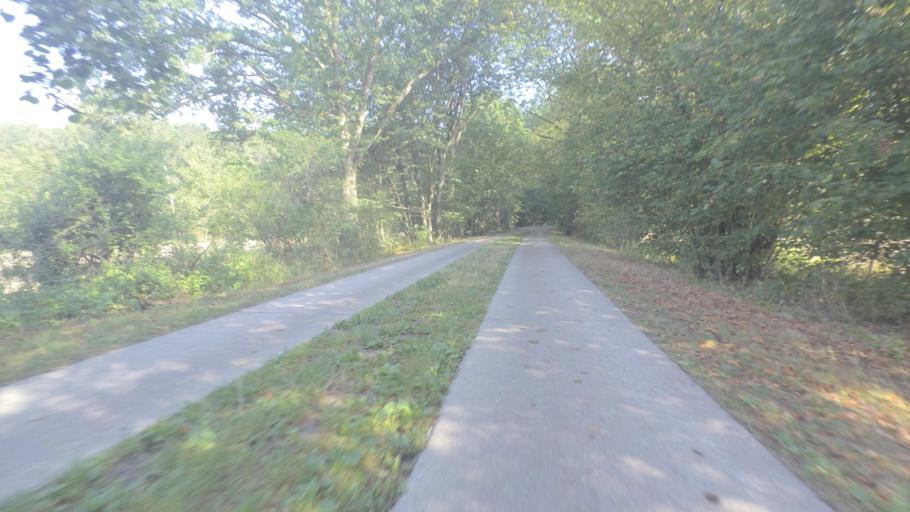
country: DE
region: Mecklenburg-Vorpommern
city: Wittenhagen
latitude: 54.1683
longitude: 13.0720
